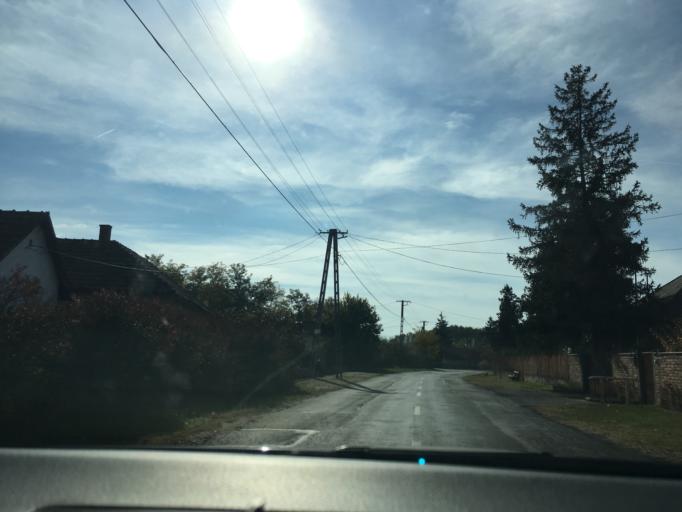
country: HU
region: Hajdu-Bihar
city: Nyirabrany
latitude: 47.5358
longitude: 22.0015
